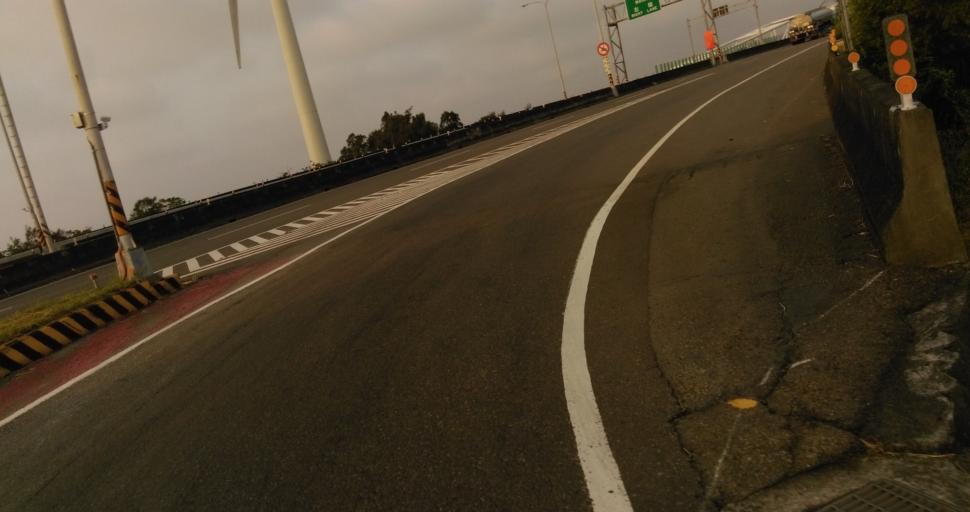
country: TW
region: Taiwan
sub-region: Hsinchu
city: Hsinchu
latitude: 24.7445
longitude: 120.8989
